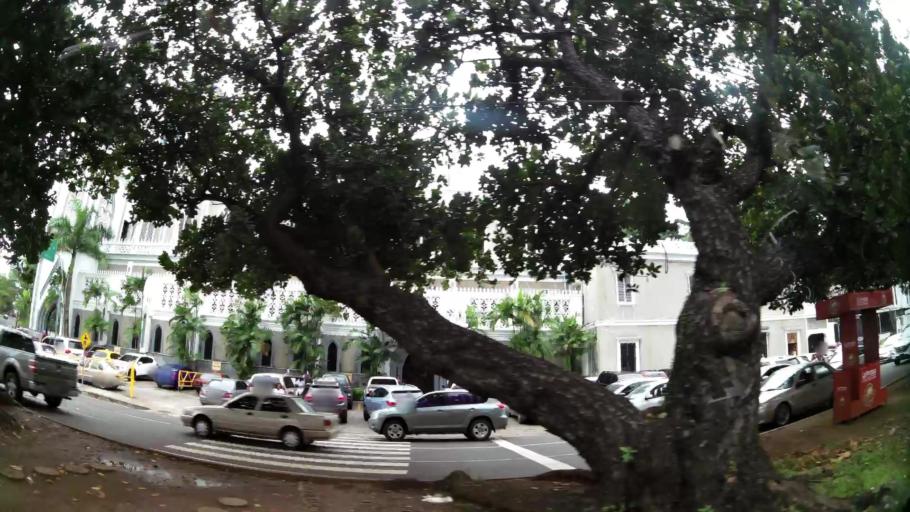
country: PA
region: Panama
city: Panama
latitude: 8.9819
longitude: -79.5283
